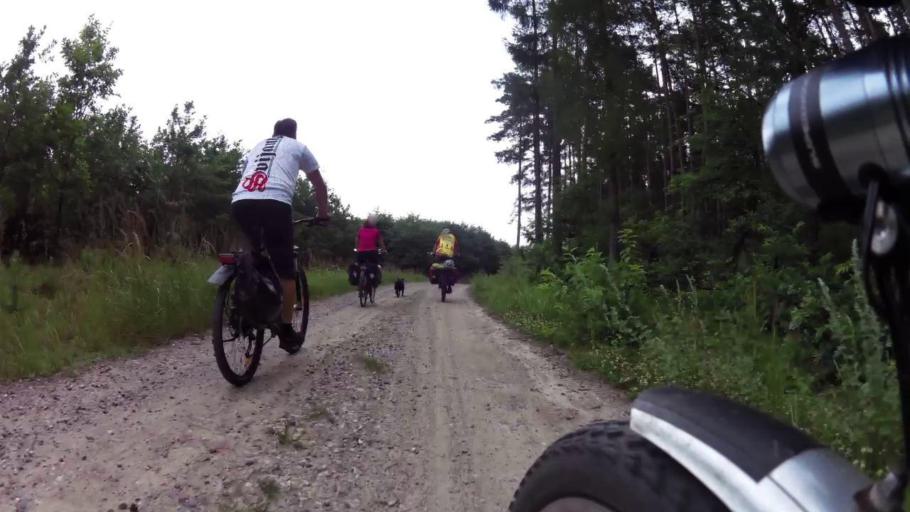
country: PL
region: West Pomeranian Voivodeship
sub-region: Powiat gryfinski
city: Mieszkowice
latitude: 52.8281
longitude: 14.5863
